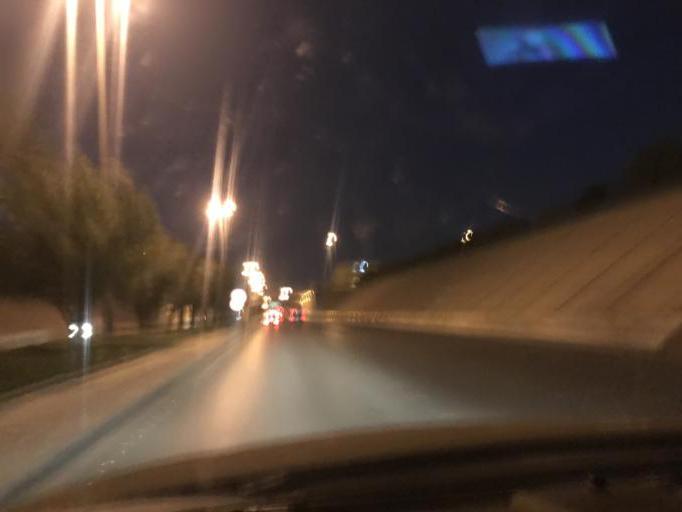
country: SA
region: Ar Riyad
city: Riyadh
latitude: 24.6673
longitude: 46.7950
